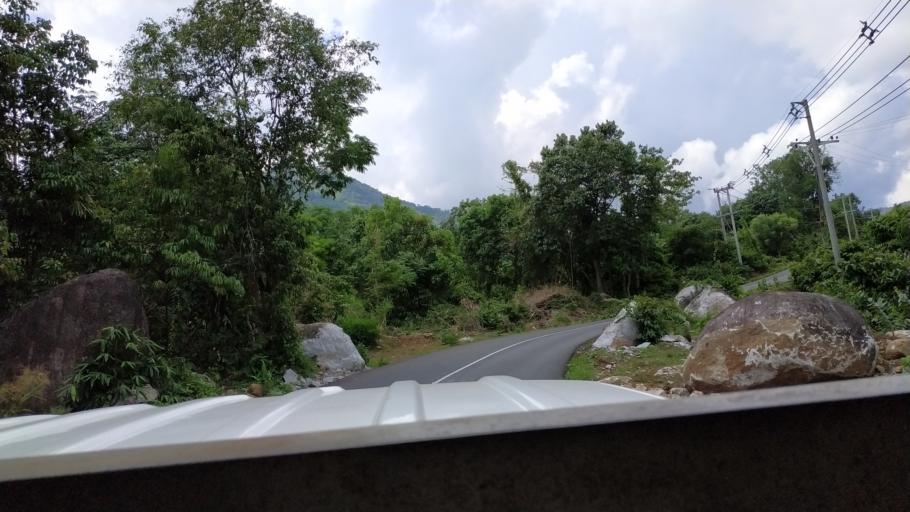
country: MM
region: Mon
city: Kyaikto
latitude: 17.4331
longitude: 97.0938
